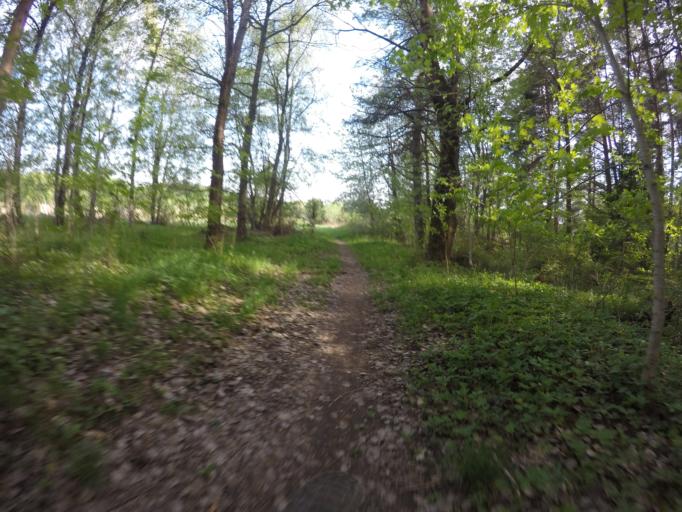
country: SE
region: Vaestmanland
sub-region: Vasteras
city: Vasteras
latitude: 59.6546
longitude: 16.5112
